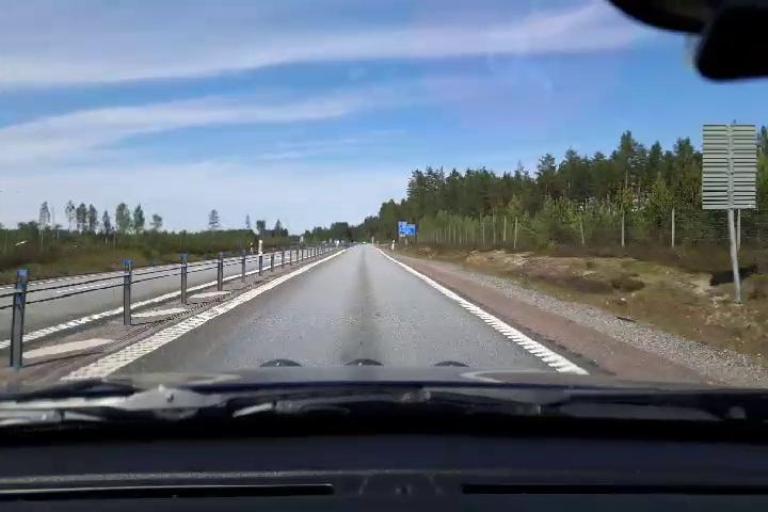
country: SE
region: Gaevleborg
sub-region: Gavle Kommun
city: Norrsundet
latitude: 61.0613
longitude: 16.9628
